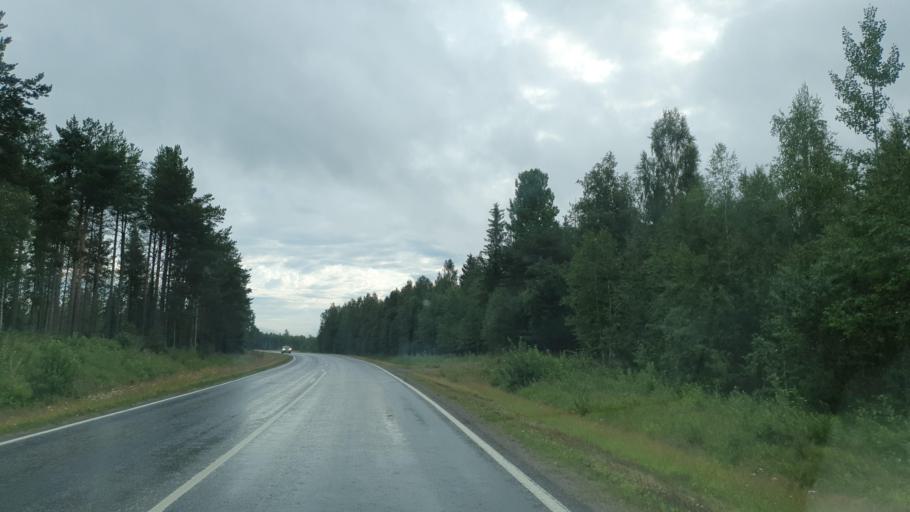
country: FI
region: Lapland
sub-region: Itae-Lappi
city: Kemijaervi
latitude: 66.8365
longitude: 27.4374
